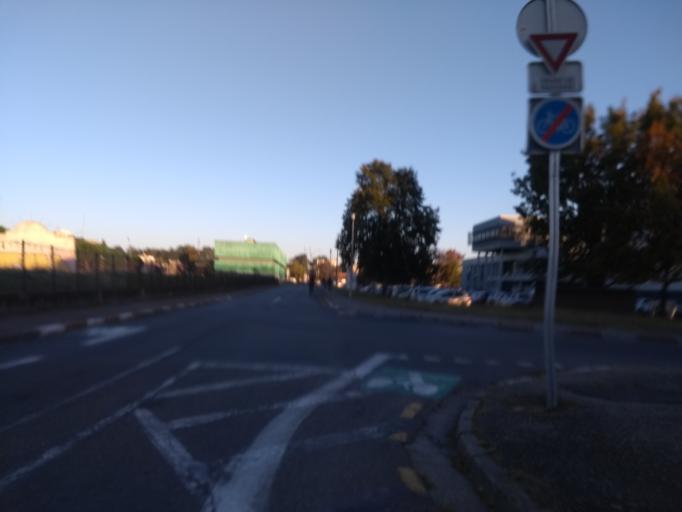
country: FR
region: Aquitaine
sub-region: Departement de la Gironde
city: Gradignan
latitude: 44.7929
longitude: -0.6149
